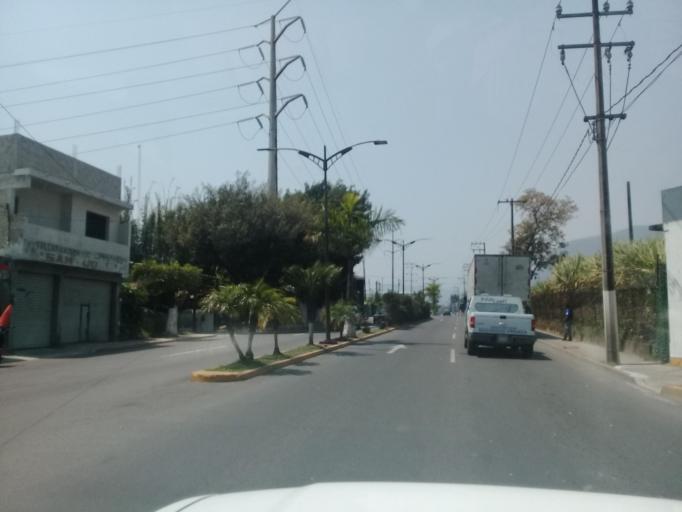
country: MX
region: Veracruz
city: Ixtac Zoquitlan
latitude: 18.8623
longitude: -97.0531
